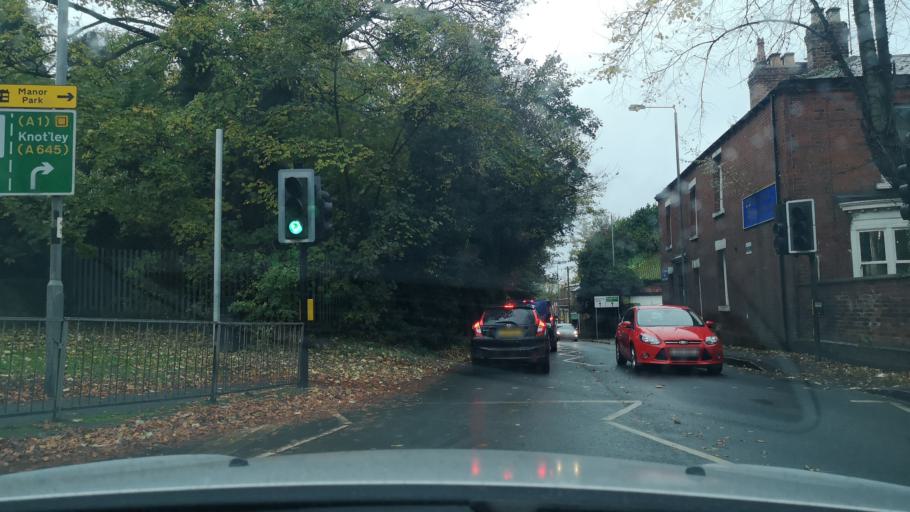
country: GB
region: England
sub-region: City and Borough of Wakefield
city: Pontefract
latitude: 53.6866
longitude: -1.3134
